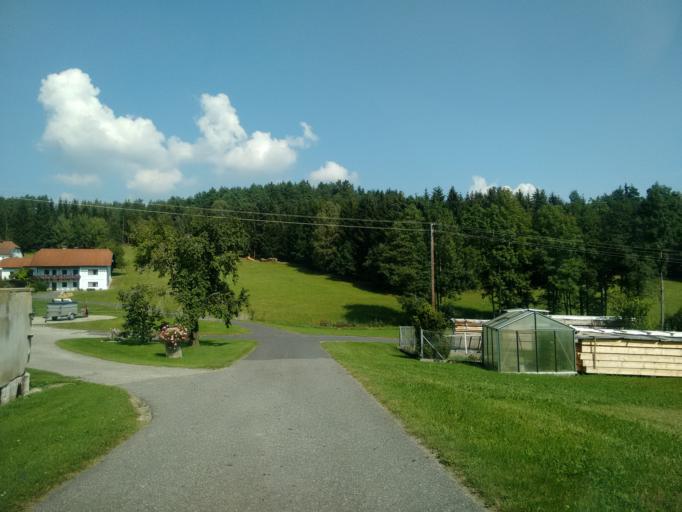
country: AT
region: Upper Austria
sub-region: Politischer Bezirk Urfahr-Umgebung
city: Haibach im Muhlkreis
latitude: 48.4119
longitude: 14.3577
